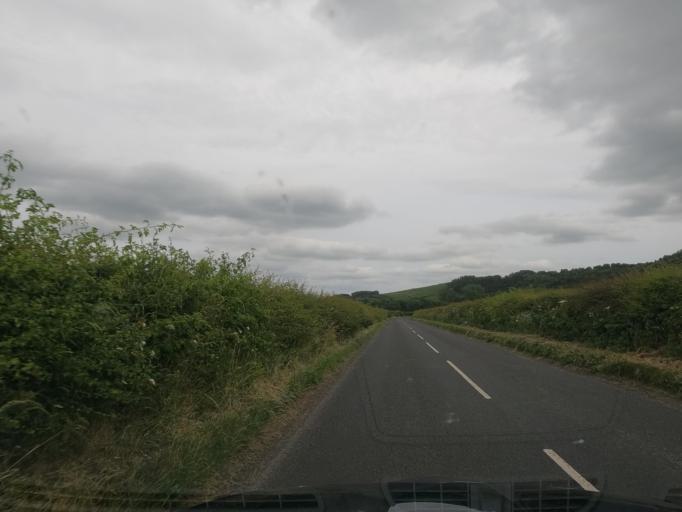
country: GB
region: England
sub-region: Northumberland
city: Doddington
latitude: 55.5558
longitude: -1.9843
